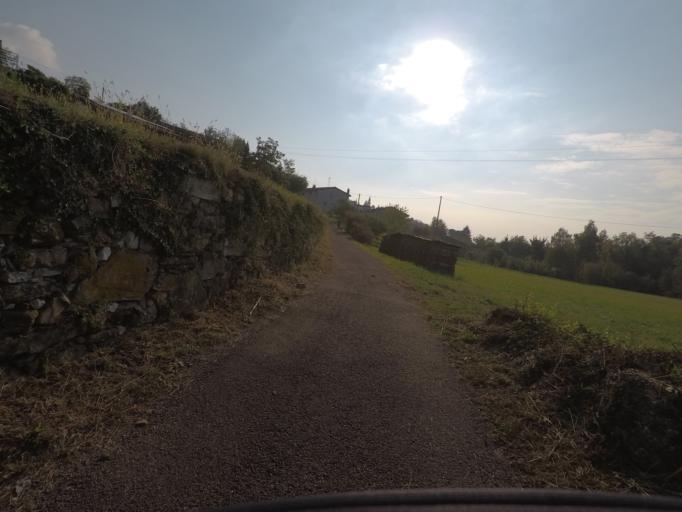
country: IT
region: Friuli Venezia Giulia
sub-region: Provincia di Udine
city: Artegna
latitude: 46.2460
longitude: 13.1467
